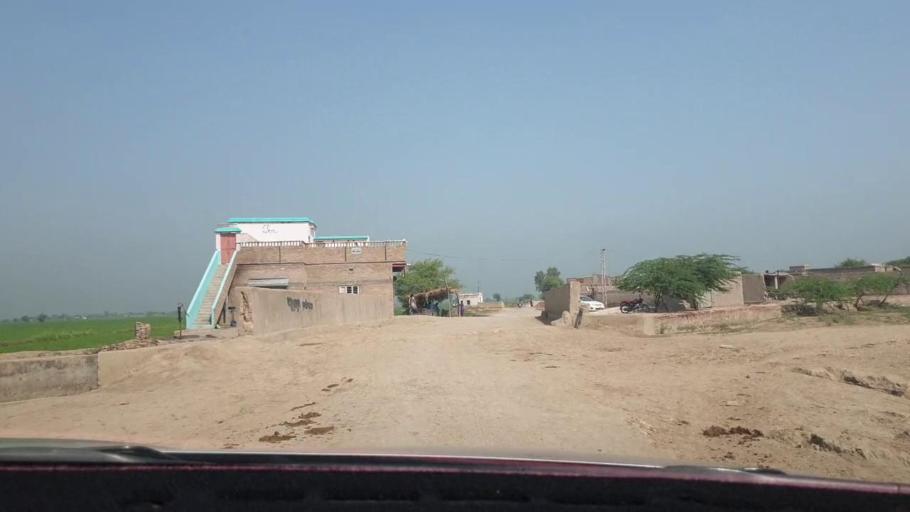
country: PK
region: Sindh
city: Nasirabad
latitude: 27.4241
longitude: 67.9054
